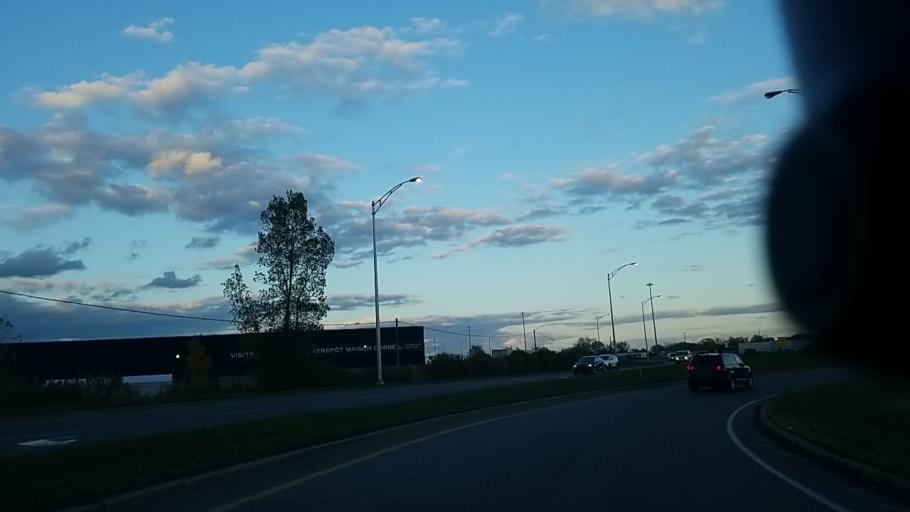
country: CA
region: Quebec
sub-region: Laval
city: Laval
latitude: 45.5871
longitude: -73.7366
